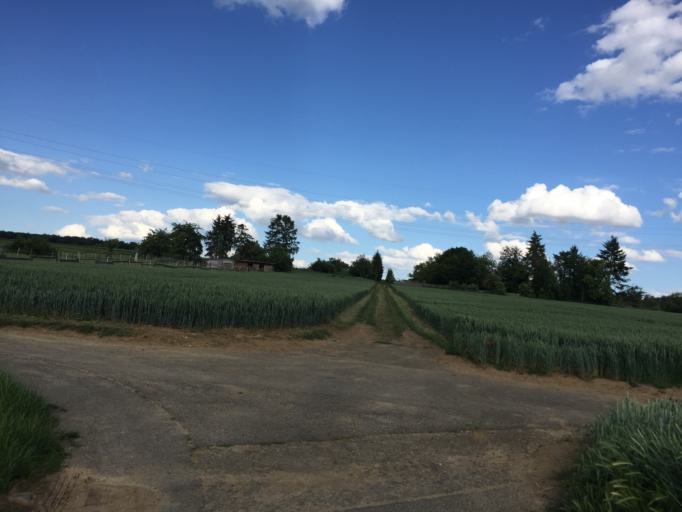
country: DE
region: Hesse
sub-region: Regierungsbezirk Darmstadt
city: Karben
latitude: 50.2337
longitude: 8.7794
